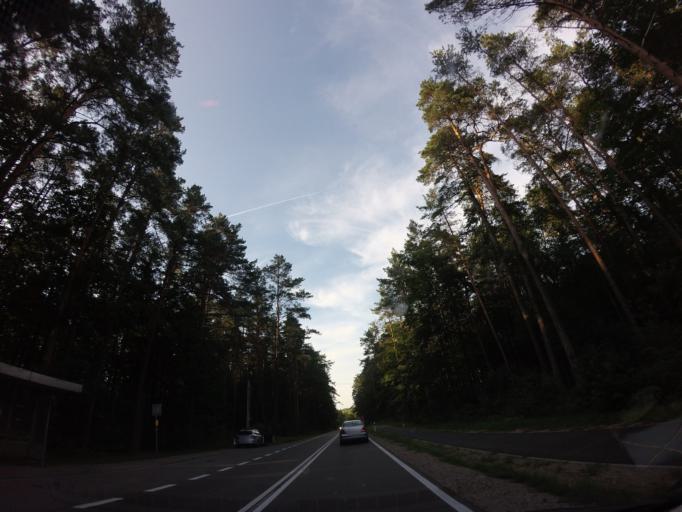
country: PL
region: Podlasie
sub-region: Powiat augustowski
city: Augustow
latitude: 53.8644
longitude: 23.0896
